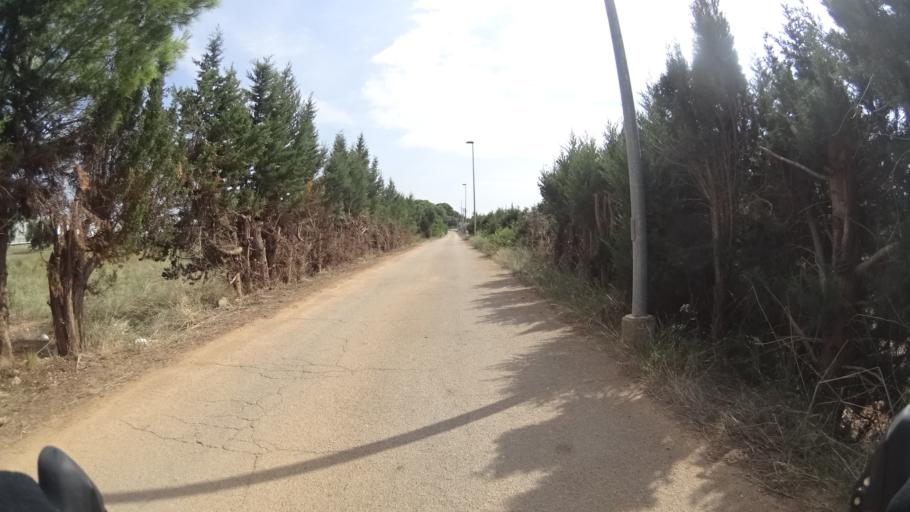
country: IT
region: Apulia
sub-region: Provincia di Lecce
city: Porto Cesareo
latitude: 40.2765
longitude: 17.9320
